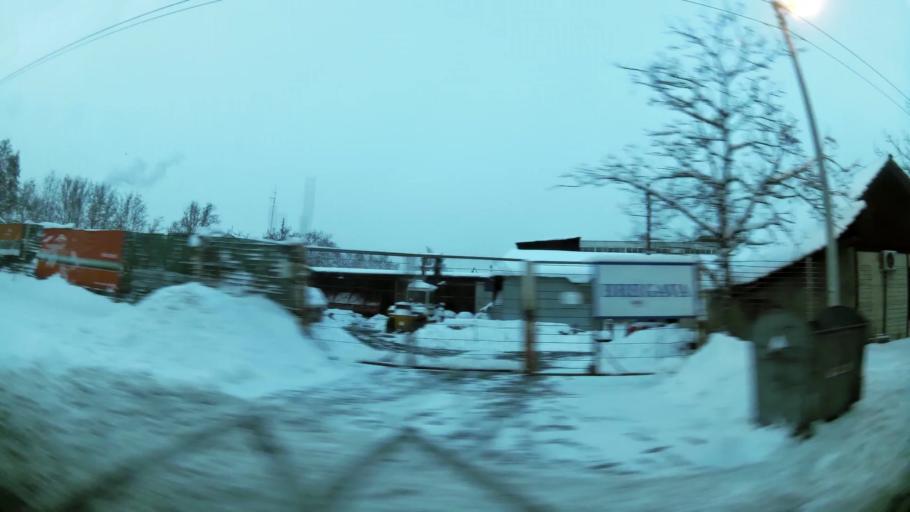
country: RS
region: Central Serbia
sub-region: Belgrade
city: Stari Grad
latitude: 44.8214
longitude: 20.4780
